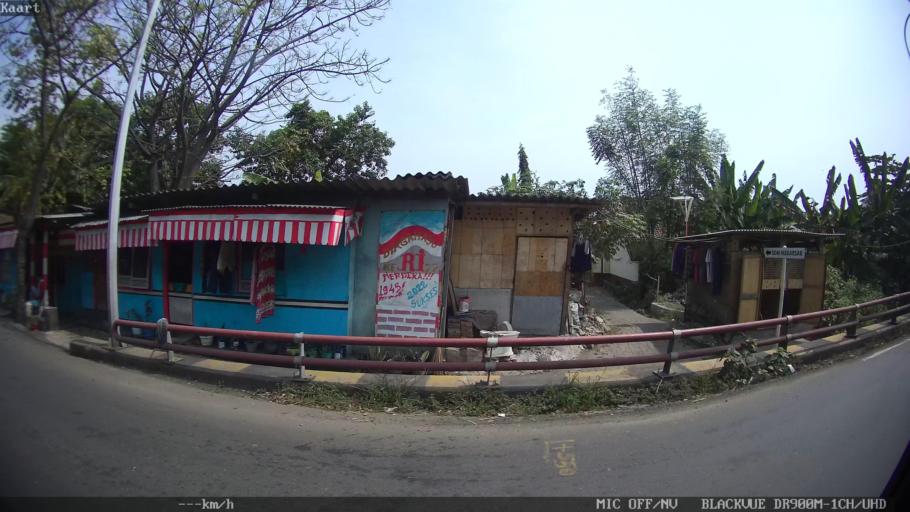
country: ID
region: Banten
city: Curug
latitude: -5.9392
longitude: 106.0032
